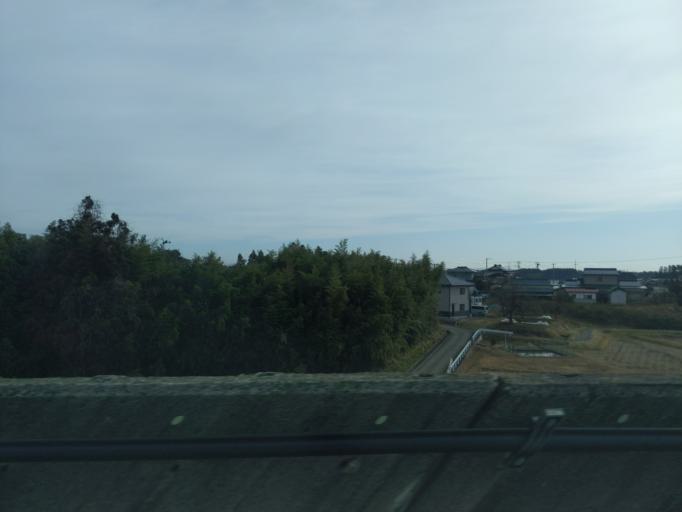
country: JP
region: Iwate
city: Ichinoseki
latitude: 38.7655
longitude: 141.0811
